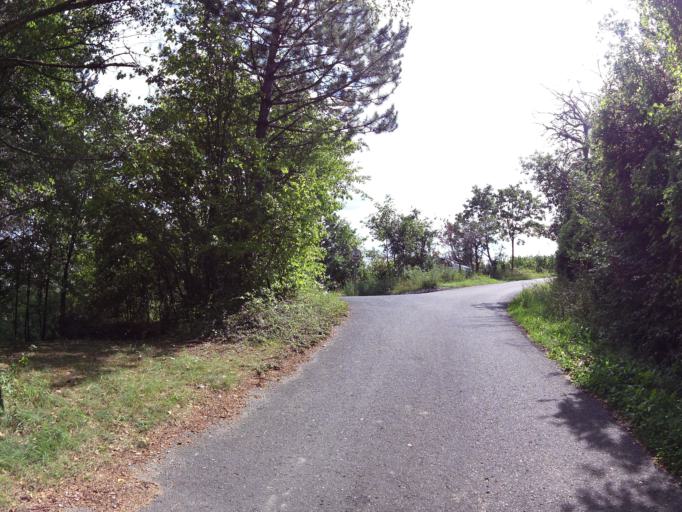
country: DE
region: Bavaria
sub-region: Regierungsbezirk Unterfranken
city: Erlabrunn
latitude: 49.8474
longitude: 9.8443
